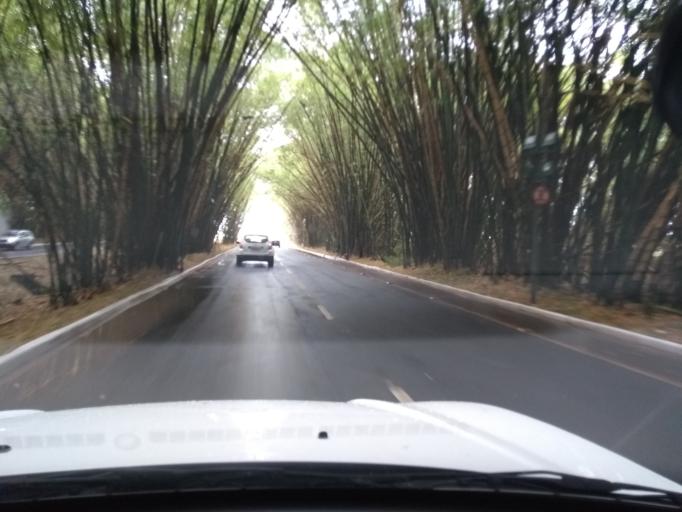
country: BR
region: Bahia
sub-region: Lauro De Freitas
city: Lauro de Freitas
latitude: -12.9094
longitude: -38.3400
